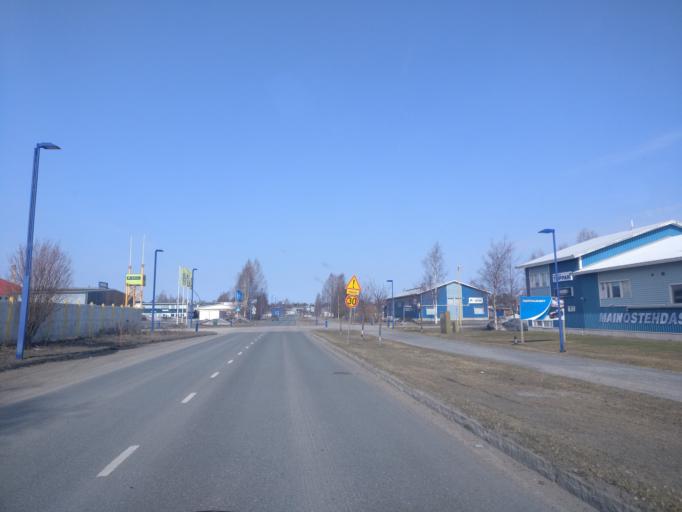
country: FI
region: Lapland
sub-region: Kemi-Tornio
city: Kemi
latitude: 65.7367
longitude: 24.5809
